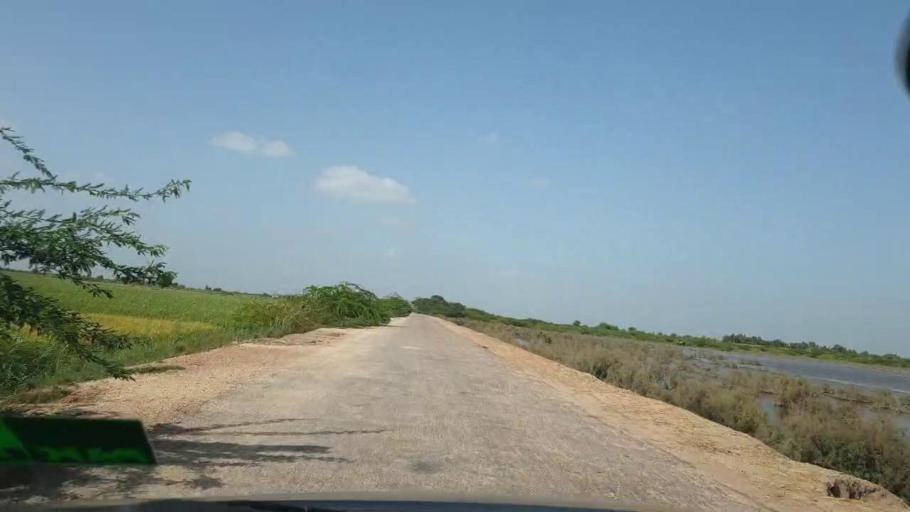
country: PK
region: Sindh
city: Tando Bago
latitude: 24.6944
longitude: 69.1896
